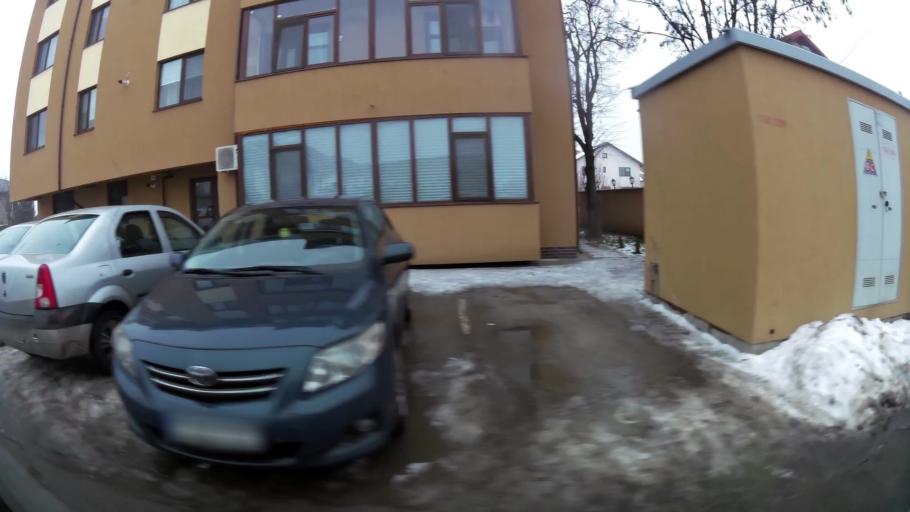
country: RO
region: Ilfov
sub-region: Comuna Chiajna
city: Rosu
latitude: 44.4462
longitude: 26.0087
